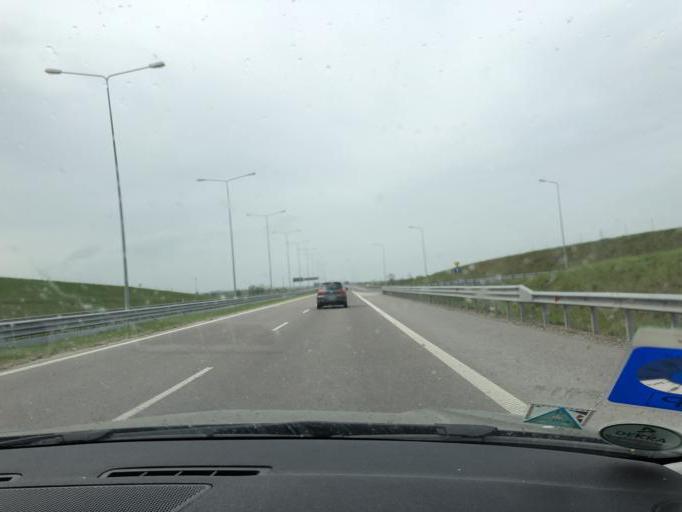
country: PL
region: Subcarpathian Voivodeship
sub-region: Powiat jaroslawski
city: Radymno
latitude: 49.9123
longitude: 22.8067
